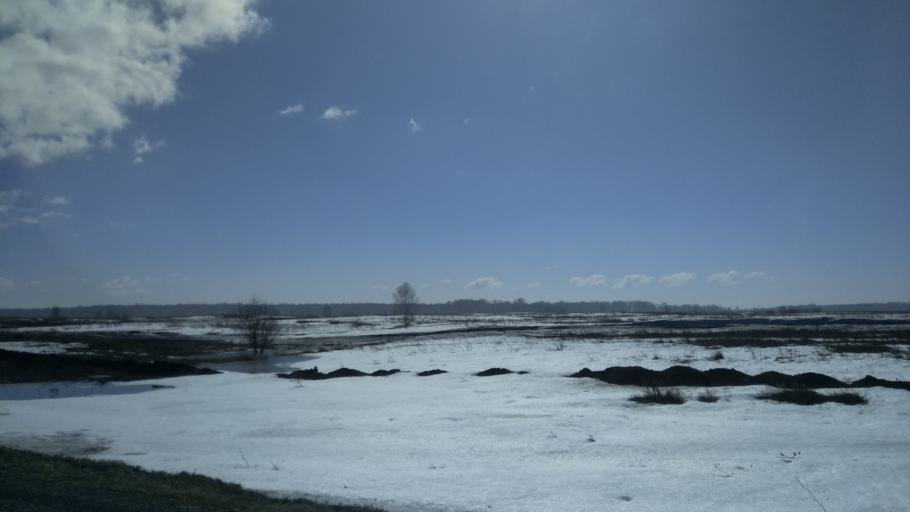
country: RU
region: Kemerovo
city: Yurga
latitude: 55.6835
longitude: 85.0025
